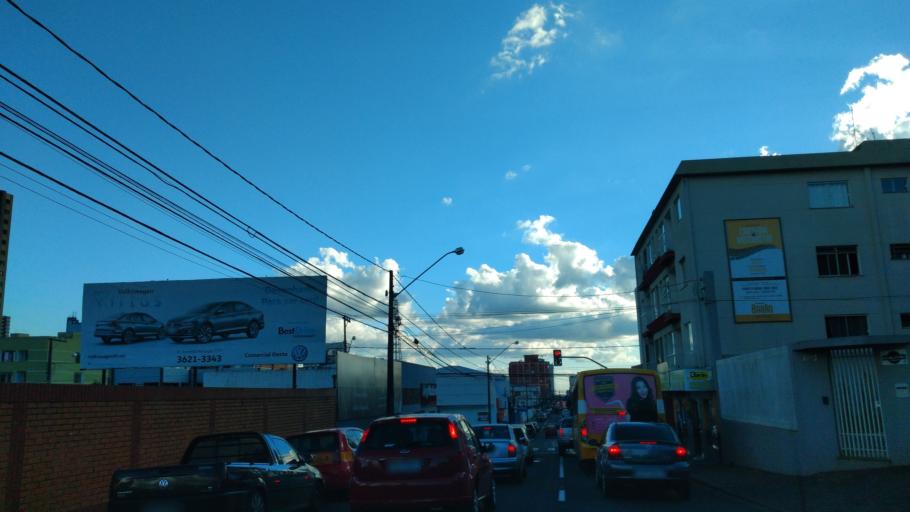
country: BR
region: Parana
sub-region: Guarapuava
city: Guarapuava
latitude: -25.3893
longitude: -51.4649
